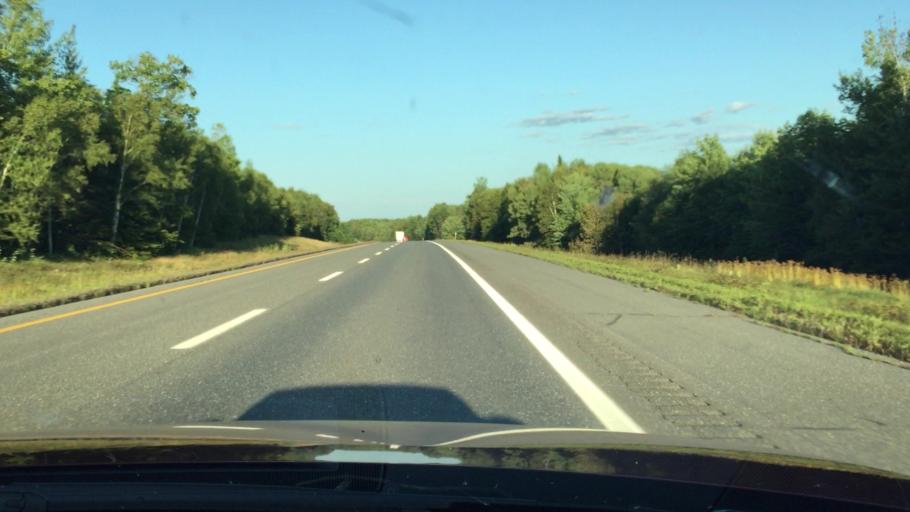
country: US
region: Maine
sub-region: Aroostook County
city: Hodgdon
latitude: 46.1402
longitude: -68.0216
